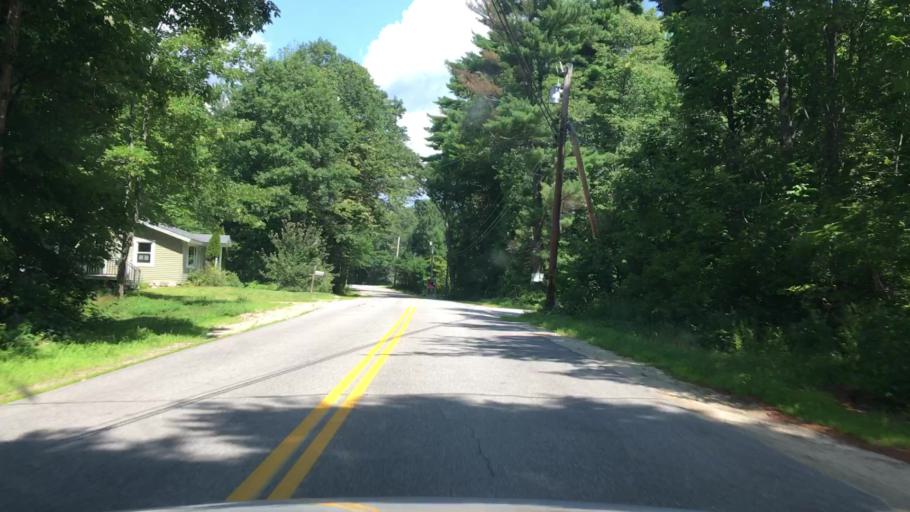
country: US
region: Maine
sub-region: Cumberland County
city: Raymond
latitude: 43.9466
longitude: -70.5255
